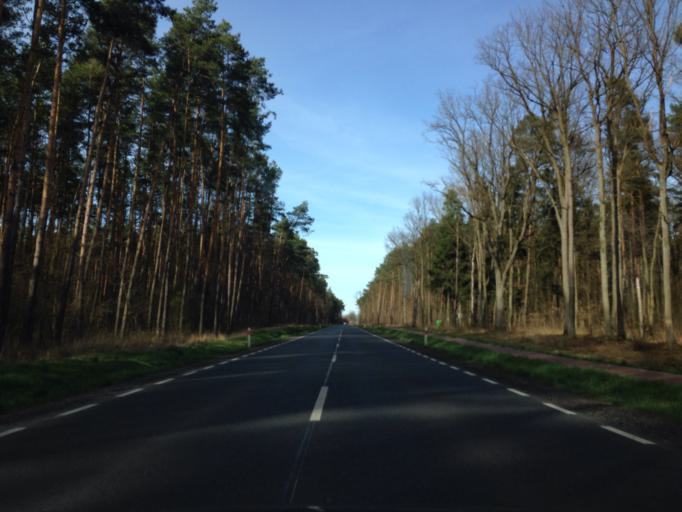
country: PL
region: Lodz Voivodeship
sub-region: Powiat poddebicki
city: Wartkowice
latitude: 51.9596
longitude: 19.0087
